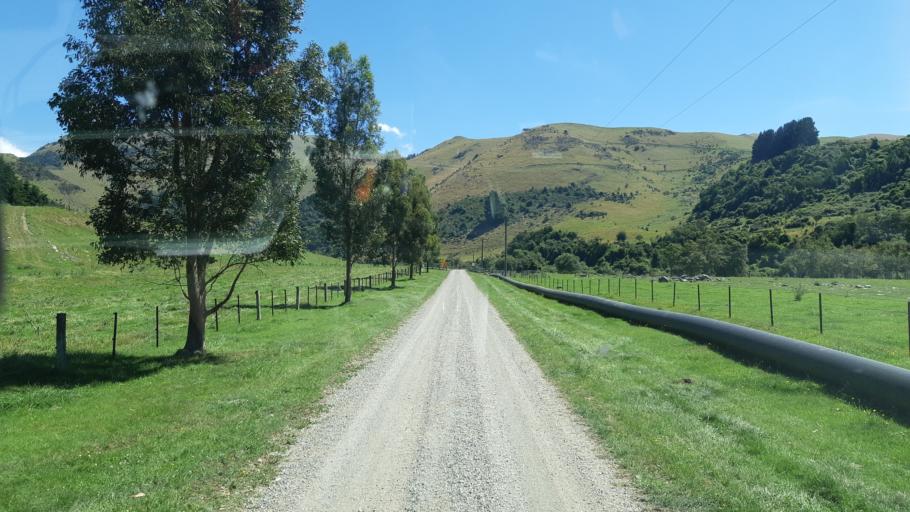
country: NZ
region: Canterbury
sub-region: Timaru District
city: Pleasant Point
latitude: -44.3339
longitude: 170.8604
